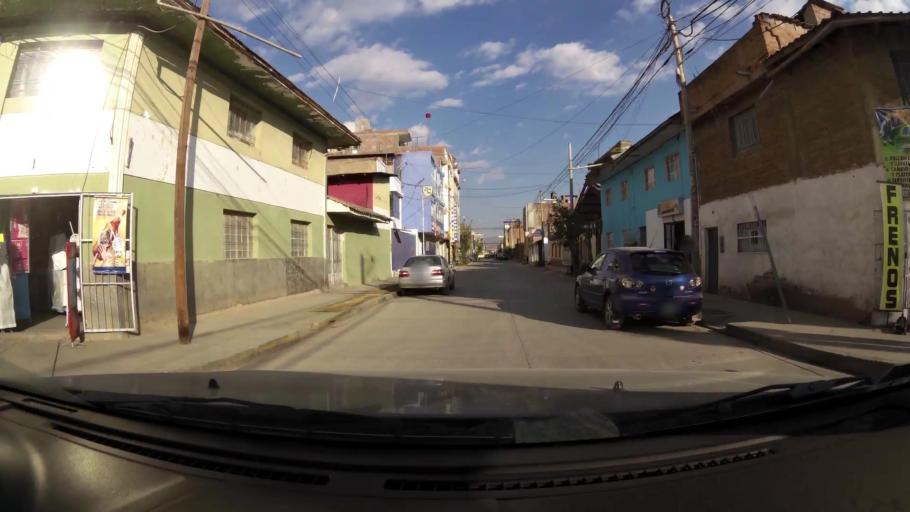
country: PE
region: Junin
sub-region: Provincia de Huancayo
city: El Tambo
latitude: -12.0516
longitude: -75.2198
